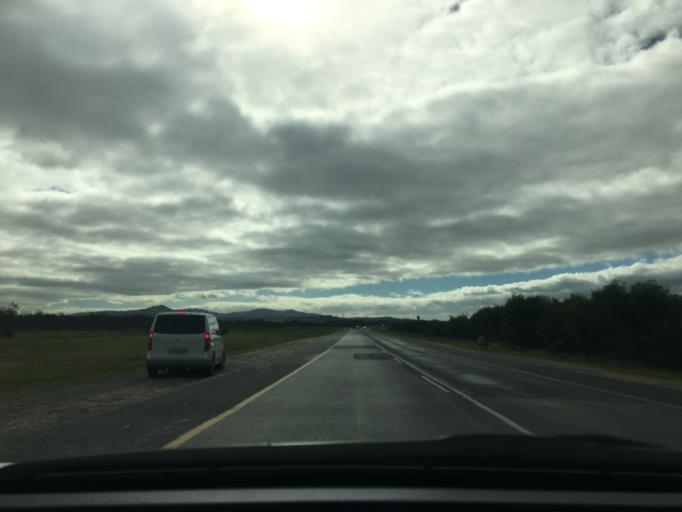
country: ZA
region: Western Cape
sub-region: Cape Winelands District Municipality
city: Stellenbosch
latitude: -34.0370
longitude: 18.7250
